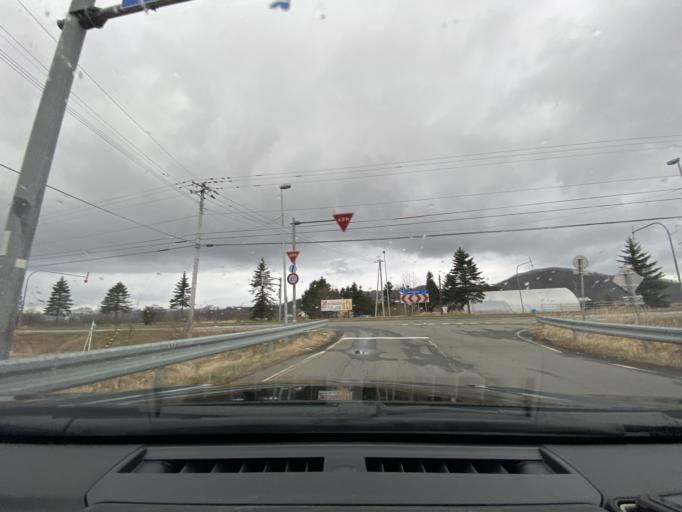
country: JP
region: Hokkaido
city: Otofuke
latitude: 43.2119
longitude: 143.5603
